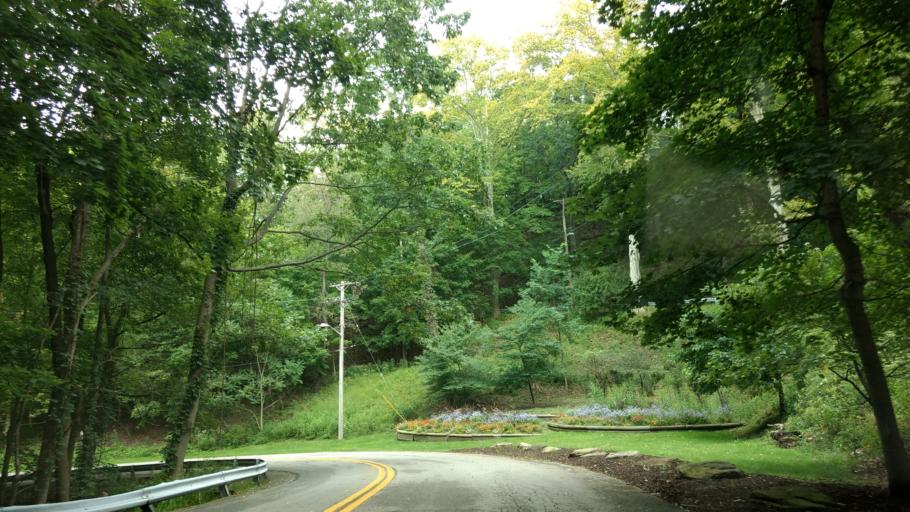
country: US
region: Pennsylvania
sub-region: Allegheny County
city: Bellevue
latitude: 40.4838
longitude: -80.0239
